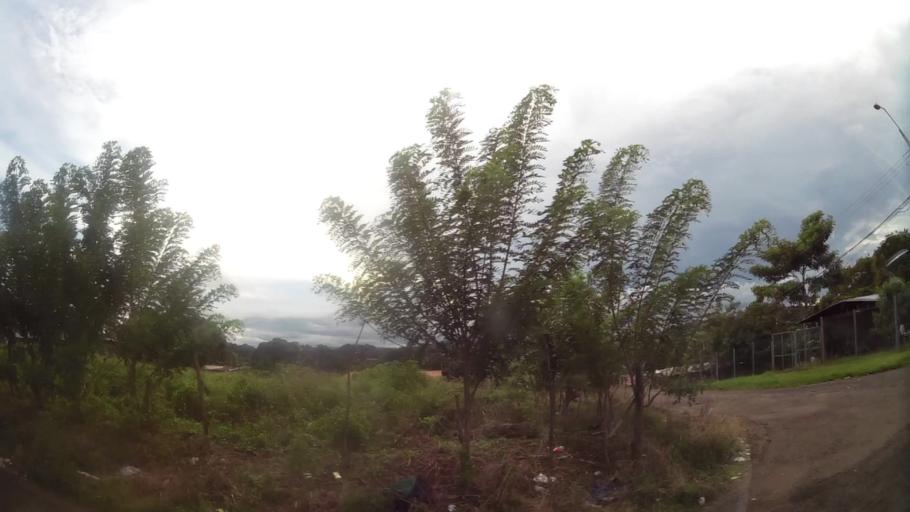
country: PA
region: Panama
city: El Coco
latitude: 8.8757
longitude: -79.8083
